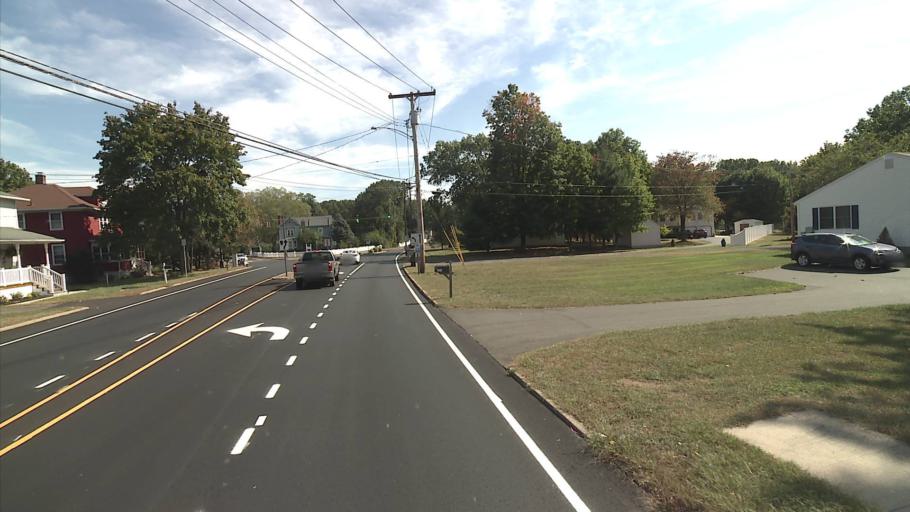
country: US
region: Connecticut
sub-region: New Haven County
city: North Haven
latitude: 41.3767
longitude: -72.8547
